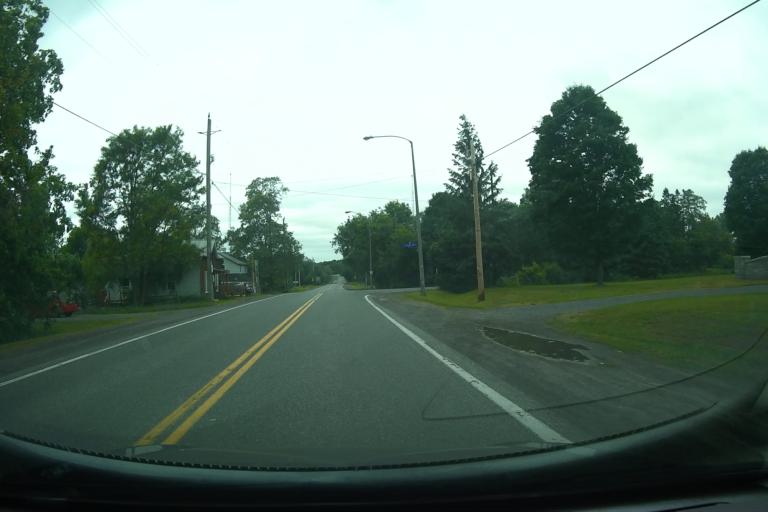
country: CA
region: Ontario
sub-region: Lanark County
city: Smiths Falls
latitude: 44.9838
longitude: -75.7997
